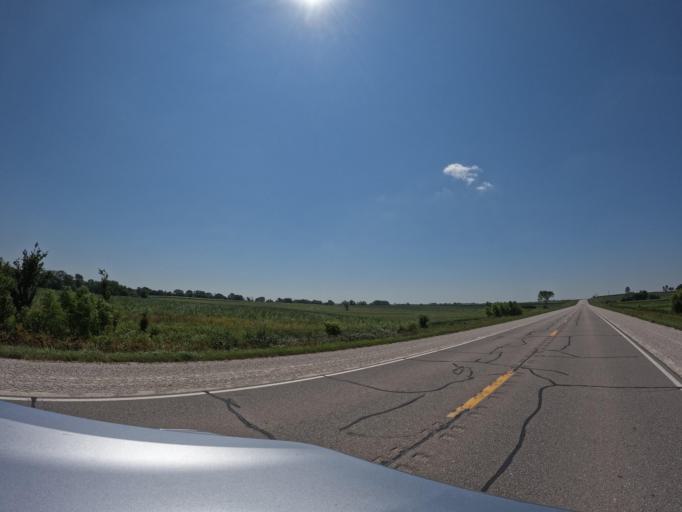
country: US
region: Iowa
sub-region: Keokuk County
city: Sigourney
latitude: 41.2963
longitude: -92.2047
